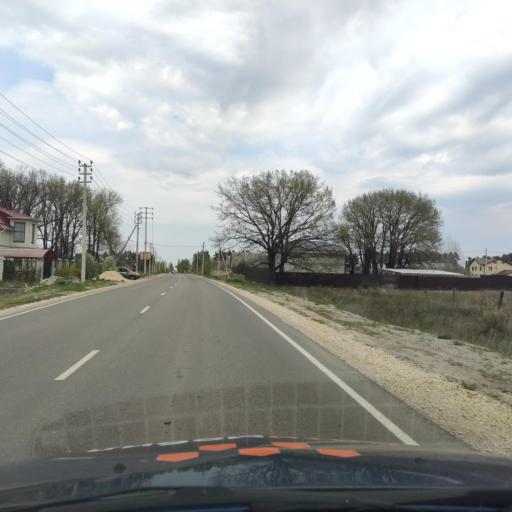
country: RU
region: Voronezj
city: Podgornoye
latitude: 51.8726
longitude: 39.1731
